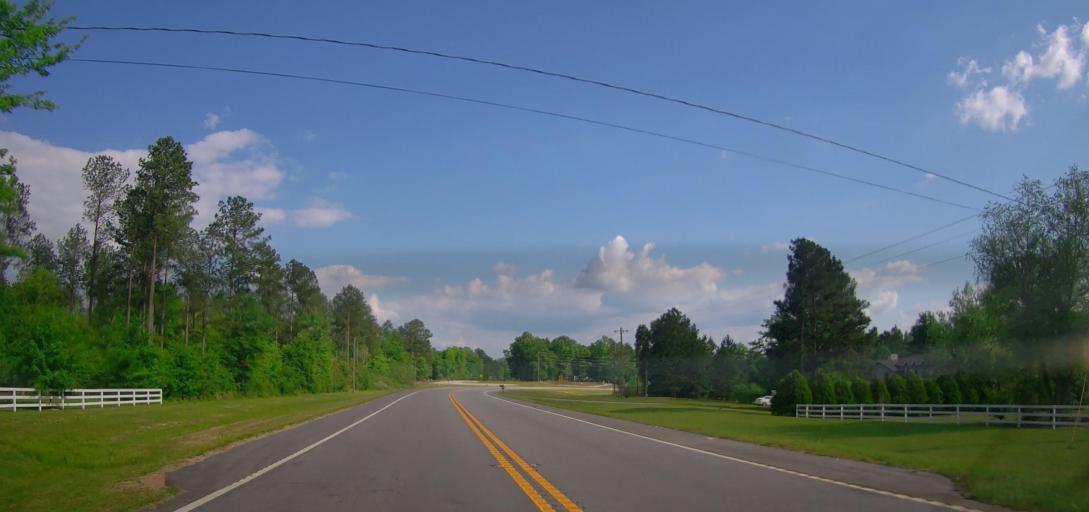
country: US
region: Georgia
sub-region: Baldwin County
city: Hardwick
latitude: 33.0424
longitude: -83.1165
